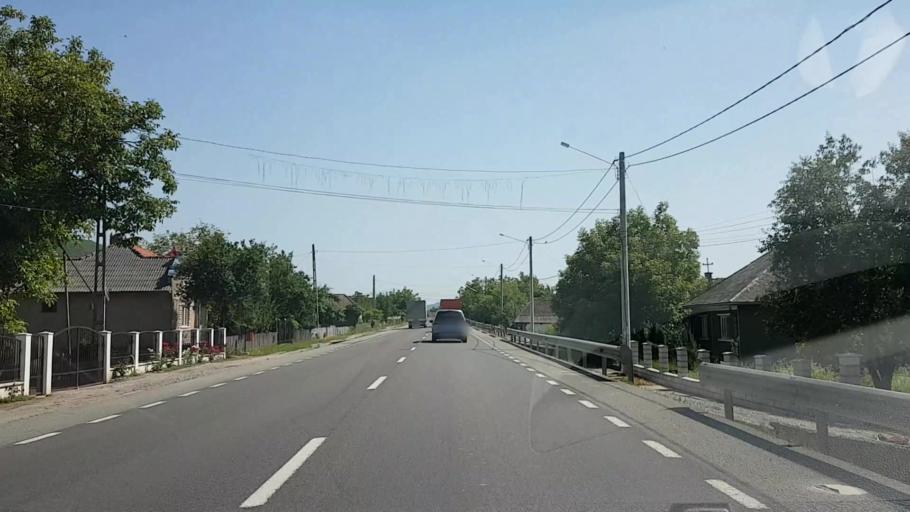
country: RO
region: Bistrita-Nasaud
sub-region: Comuna Sieu-Odorhei
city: Sieu-Odorhei
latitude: 47.1528
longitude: 24.3060
